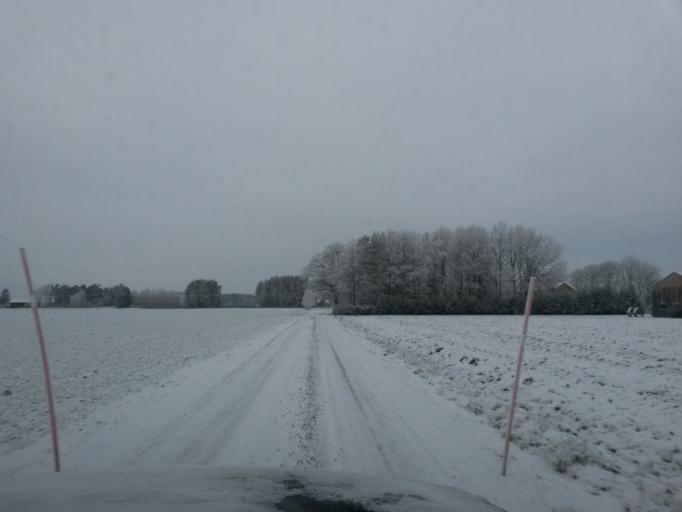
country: SE
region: Vaestra Goetaland
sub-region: Grastorps Kommun
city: Graestorp
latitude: 58.3744
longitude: 12.8234
